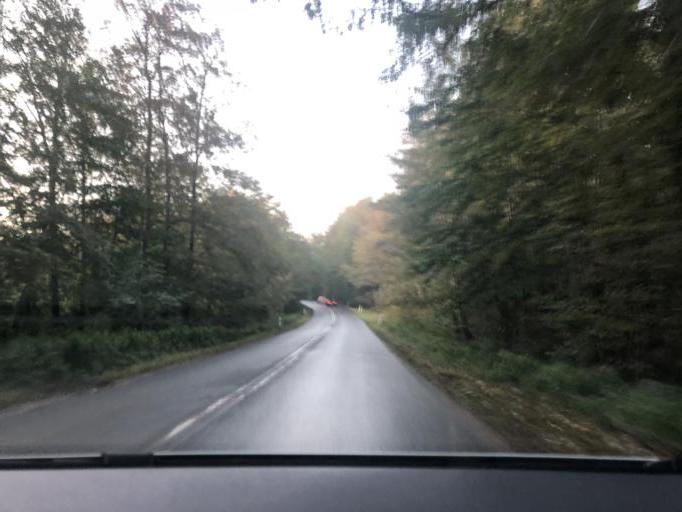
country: DK
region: Capital Region
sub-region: Frederikssund Kommune
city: Slangerup
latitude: 55.8134
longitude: 12.2063
